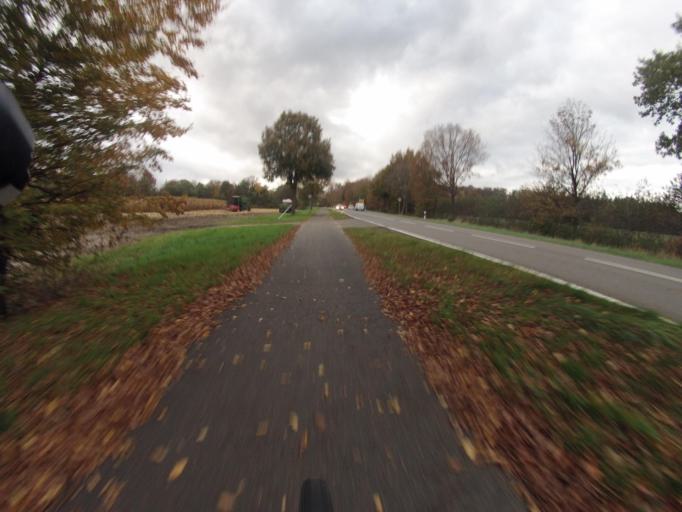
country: DE
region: North Rhine-Westphalia
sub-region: Regierungsbezirk Munster
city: Birgte
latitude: 52.2860
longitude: 7.6306
